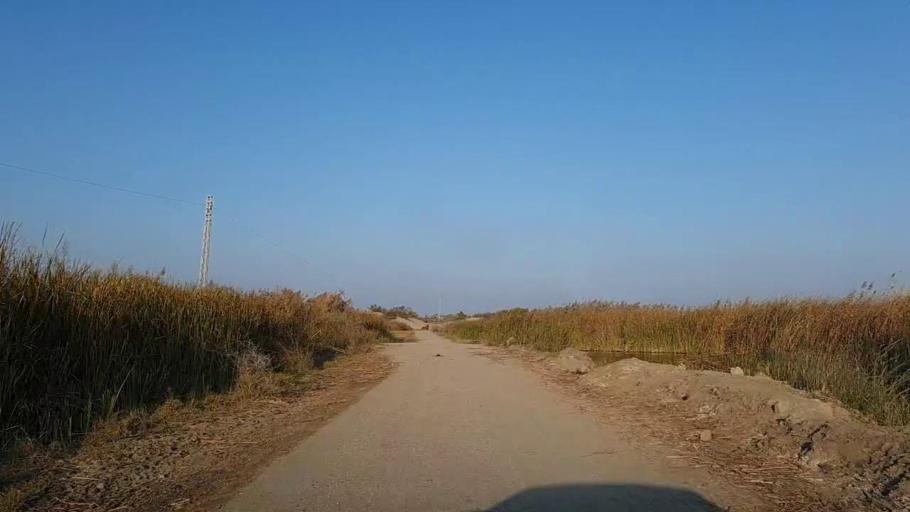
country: PK
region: Sindh
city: Sanghar
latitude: 26.2997
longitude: 68.9907
